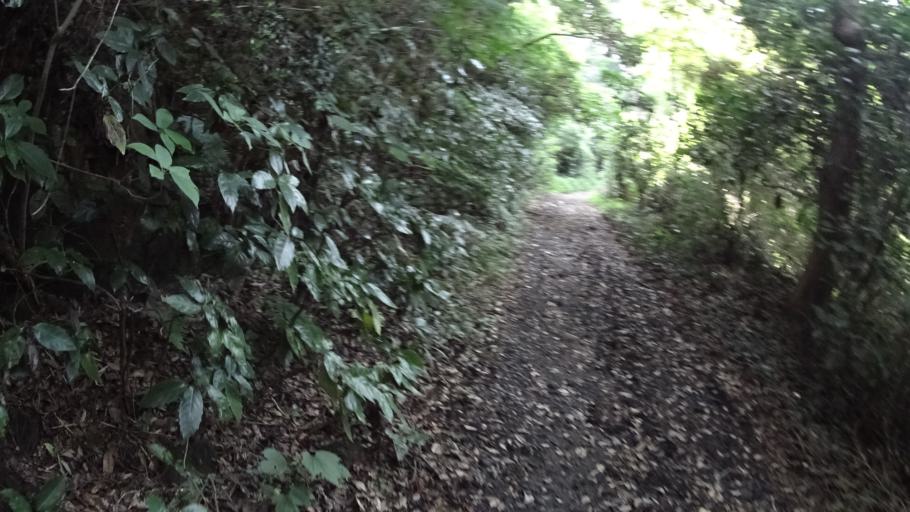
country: JP
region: Kanagawa
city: Zushi
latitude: 35.3134
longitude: 139.6062
